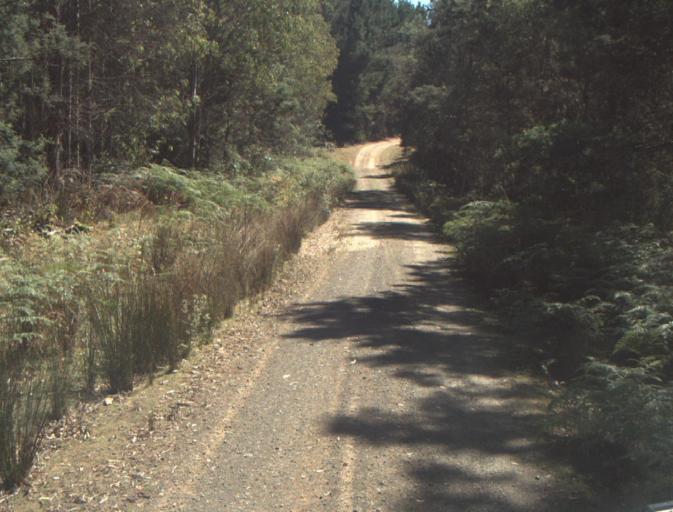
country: AU
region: Tasmania
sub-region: Dorset
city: Scottsdale
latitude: -41.2540
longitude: 147.3456
